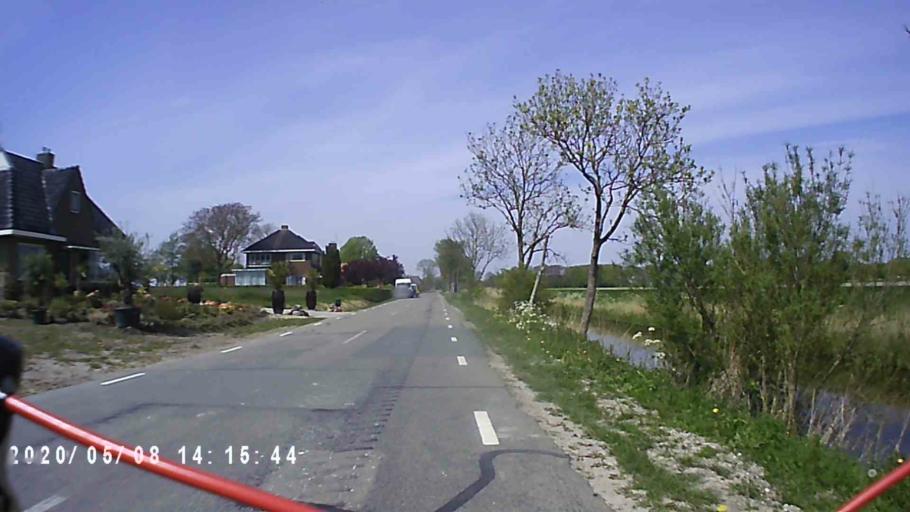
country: NL
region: Groningen
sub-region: Gemeente Appingedam
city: Appingedam
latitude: 53.3581
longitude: 6.7831
